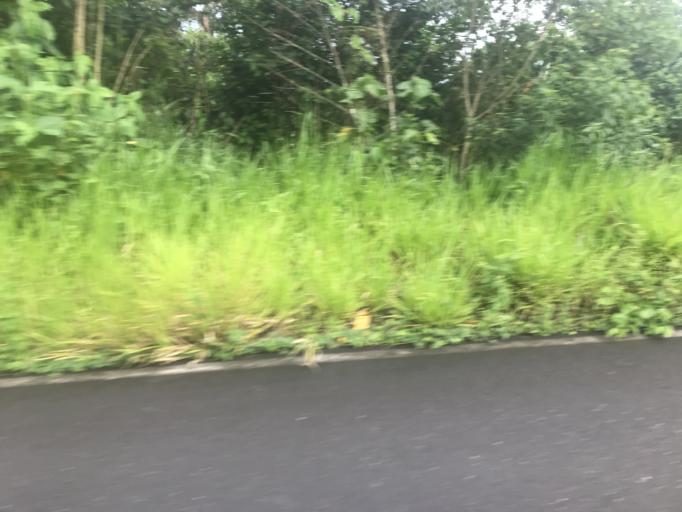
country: EC
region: Napo
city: Tena
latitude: -1.0423
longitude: -77.8049
